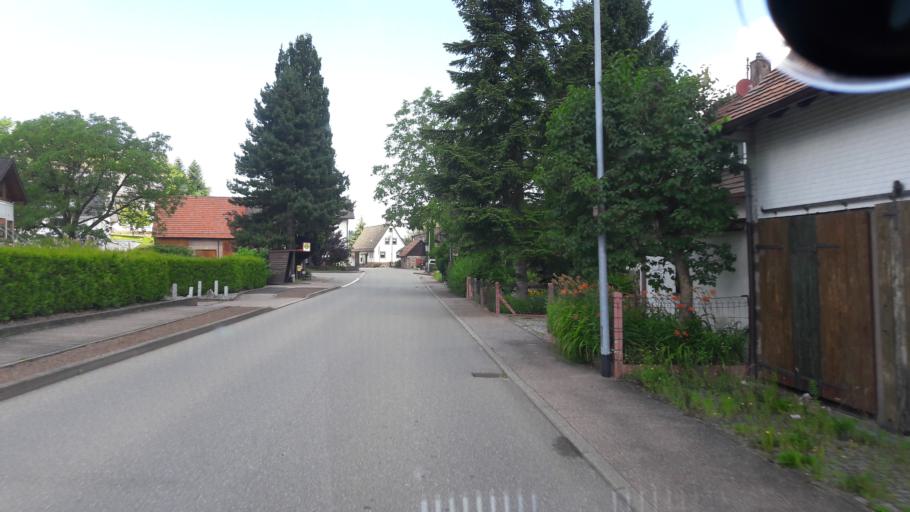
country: DE
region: Baden-Wuerttemberg
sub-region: Karlsruhe Region
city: Bad Herrenalb
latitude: 48.8312
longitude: 8.3944
